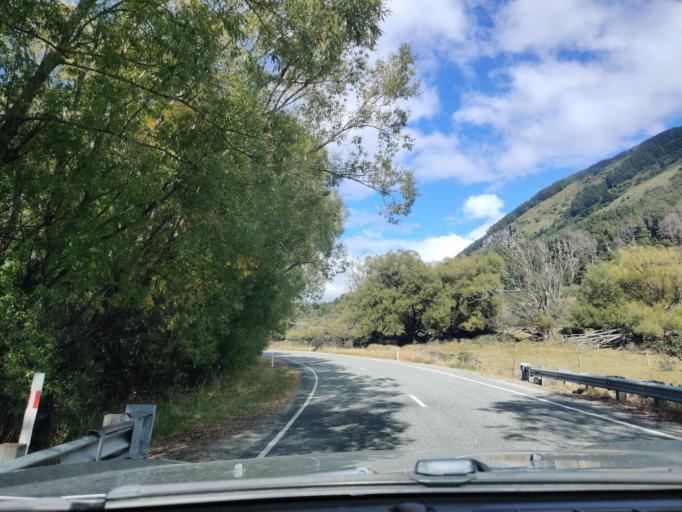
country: NZ
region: Otago
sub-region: Queenstown-Lakes District
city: Queenstown
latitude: -44.7878
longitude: 168.3878
